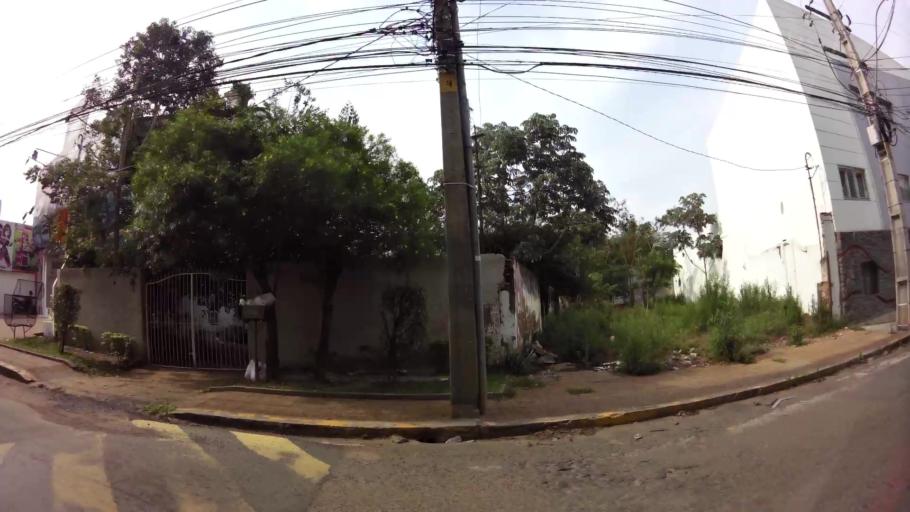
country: PY
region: Central
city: Fernando de la Mora
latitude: -25.2817
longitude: -57.5661
